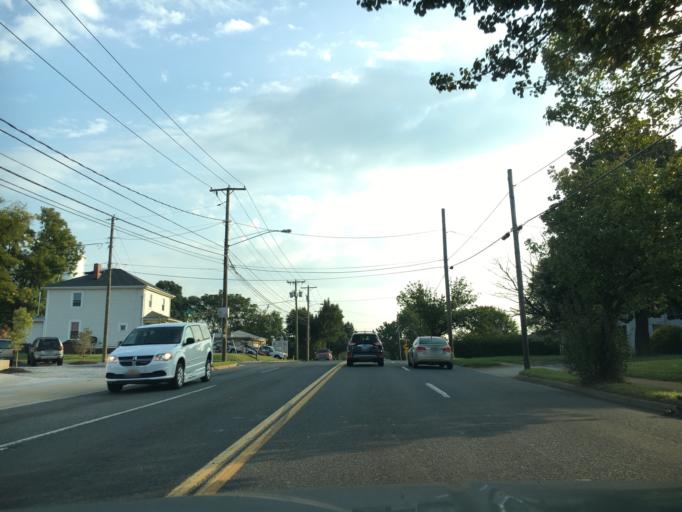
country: US
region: Virginia
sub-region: City of Lynchburg
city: West Lynchburg
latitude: 37.3803
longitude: -79.1824
